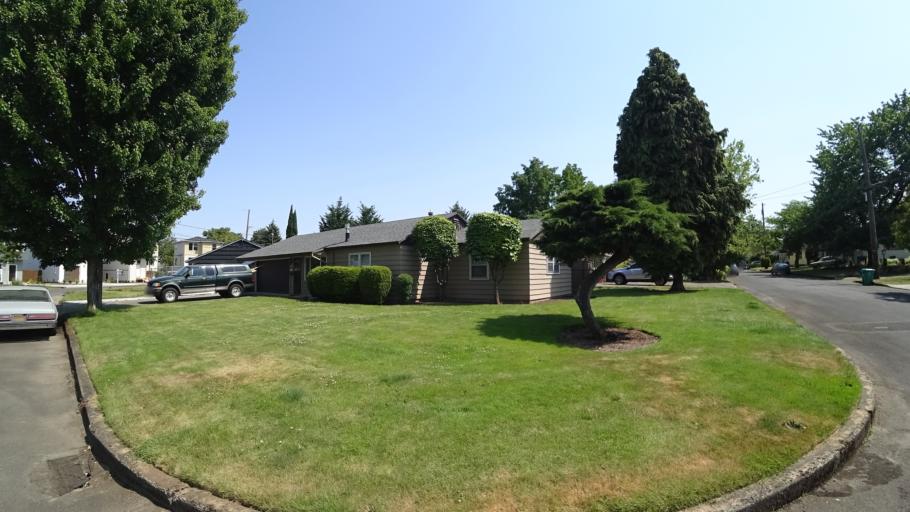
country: US
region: Oregon
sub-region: Multnomah County
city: Portland
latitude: 45.5820
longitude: -122.7044
